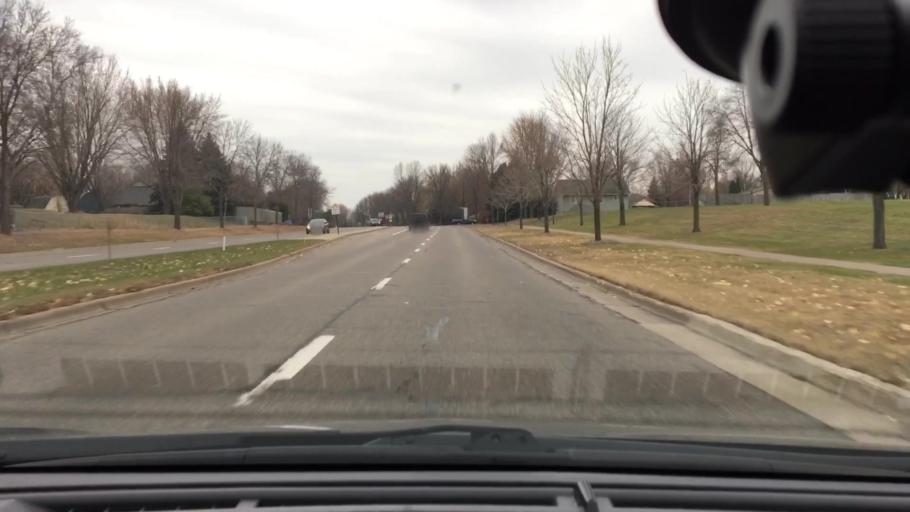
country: US
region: Minnesota
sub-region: Hennepin County
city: Maple Grove
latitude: 45.1150
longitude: -93.4521
